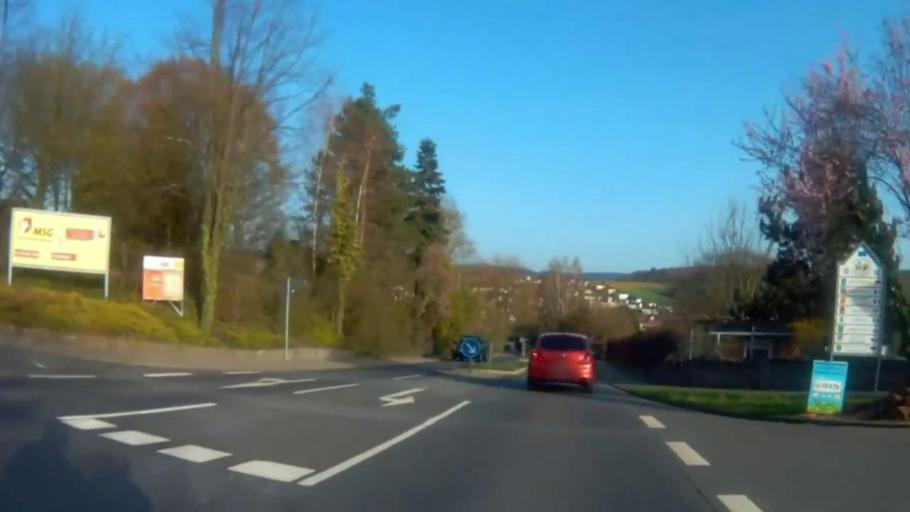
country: DE
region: Hesse
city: Gross-Bieberau
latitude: 49.7990
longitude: 8.8167
